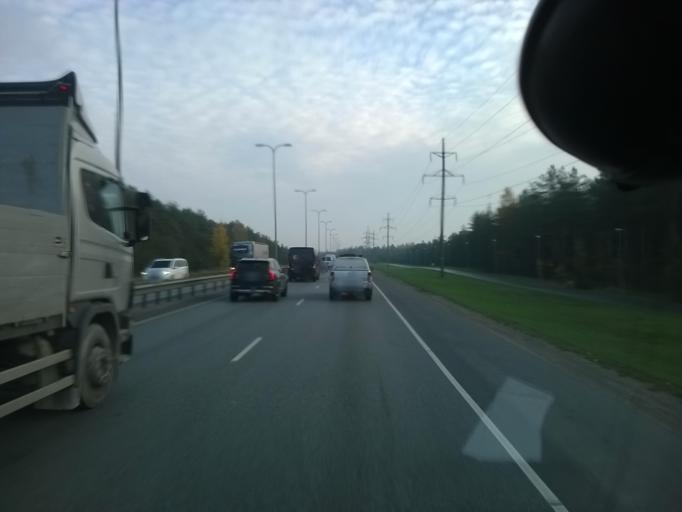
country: EE
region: Harju
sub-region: Tallinna linn
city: Tallinn
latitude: 59.4081
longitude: 24.7481
